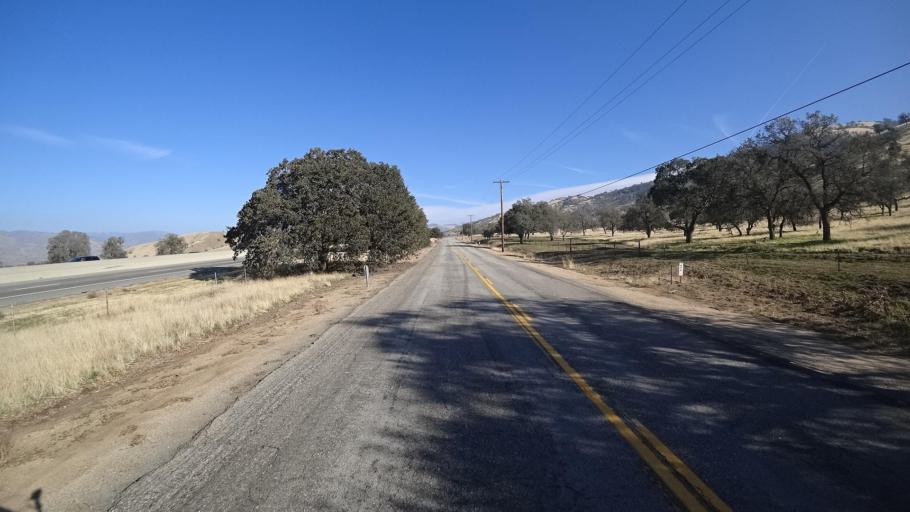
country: US
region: California
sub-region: Kern County
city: Bear Valley Springs
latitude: 35.2638
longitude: -118.6532
